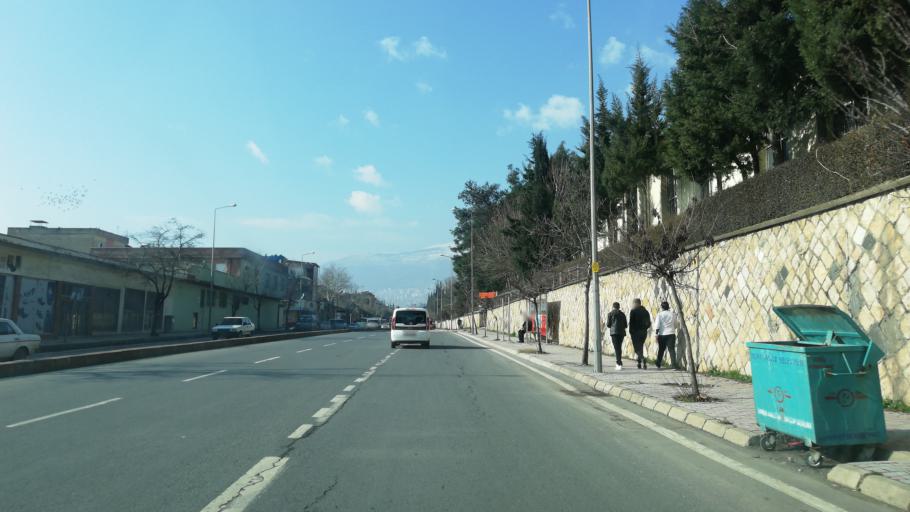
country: TR
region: Kahramanmaras
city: Kahramanmaras
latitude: 37.5727
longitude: 36.9402
